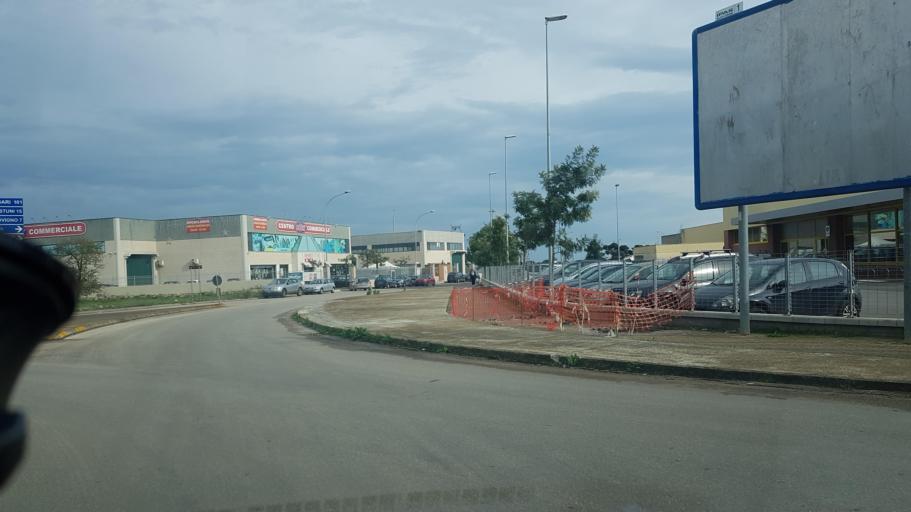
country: IT
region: Apulia
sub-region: Provincia di Brindisi
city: San Vito dei Normanni
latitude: 40.6652
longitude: 17.6993
